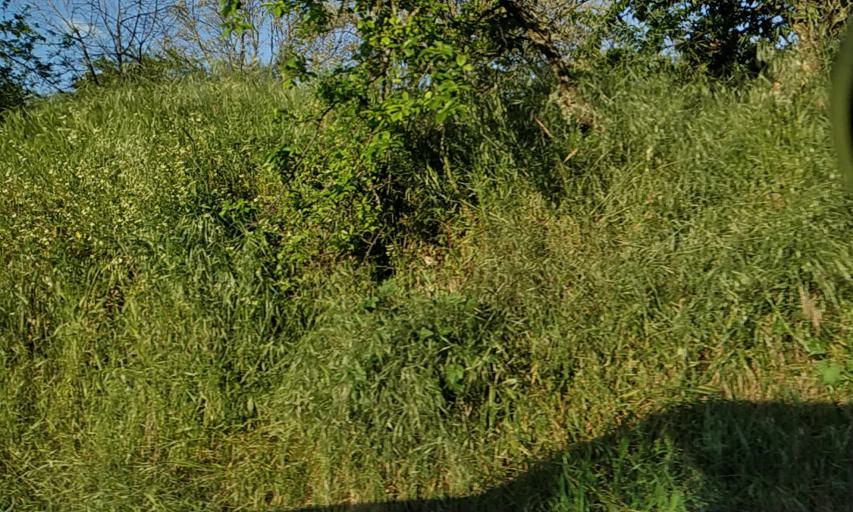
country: PT
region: Portalegre
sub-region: Marvao
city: Marvao
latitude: 39.3651
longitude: -7.4036
